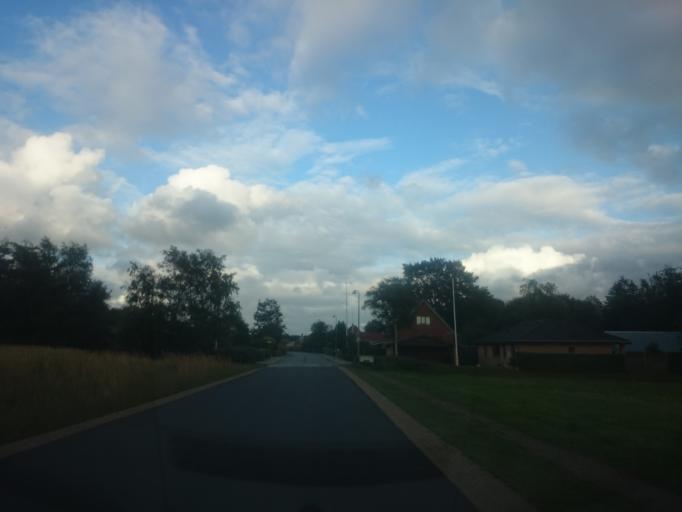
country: DK
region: South Denmark
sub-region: Billund Kommune
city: Billund
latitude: 55.6296
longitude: 9.0708
